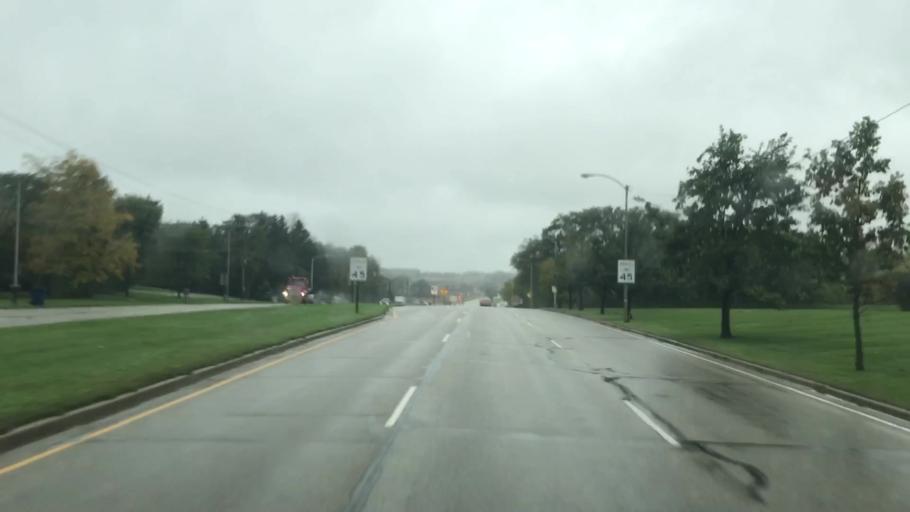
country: US
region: Wisconsin
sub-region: Waukesha County
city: Menomonee Falls
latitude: 43.1772
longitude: -88.0583
